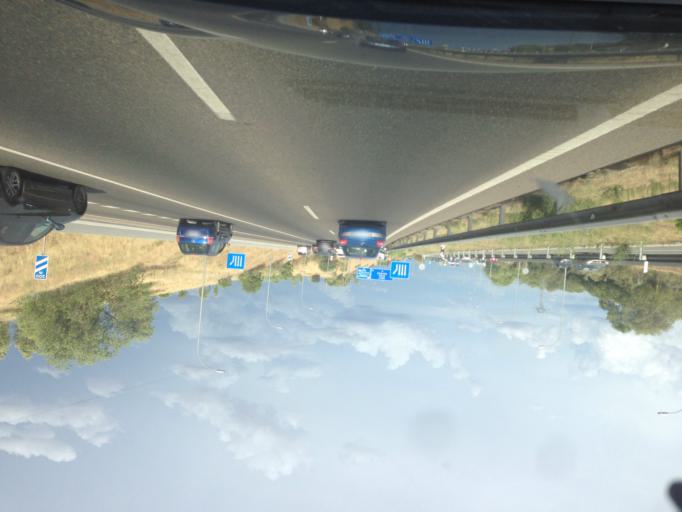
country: ES
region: Madrid
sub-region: Provincia de Madrid
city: Alcobendas
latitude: 40.5329
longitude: -3.6334
